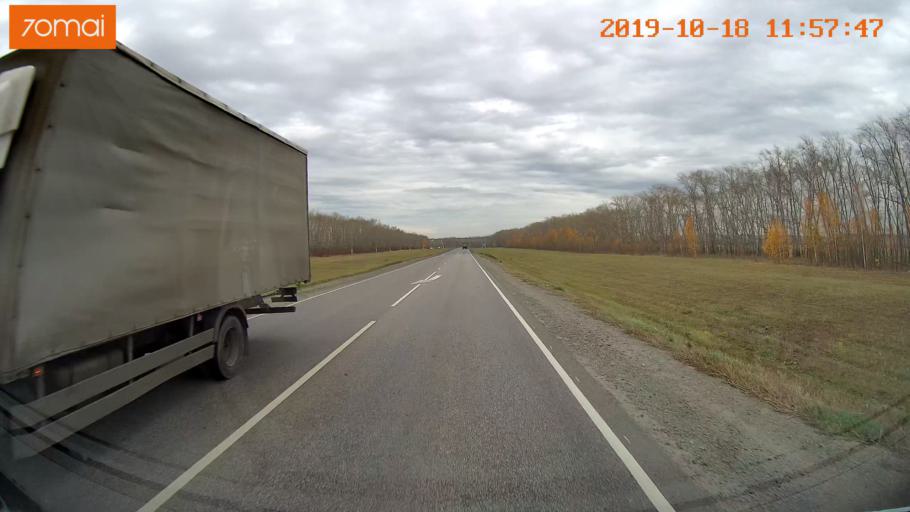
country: RU
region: Rjazan
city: Mikhaylov
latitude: 54.2673
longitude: 39.1526
